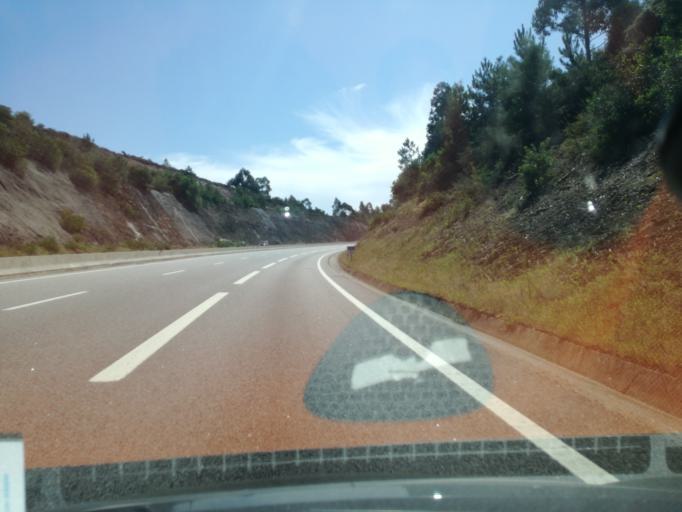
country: PT
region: Viana do Castelo
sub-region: Viana do Castelo
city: Meadela
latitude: 41.7778
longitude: -8.7846
